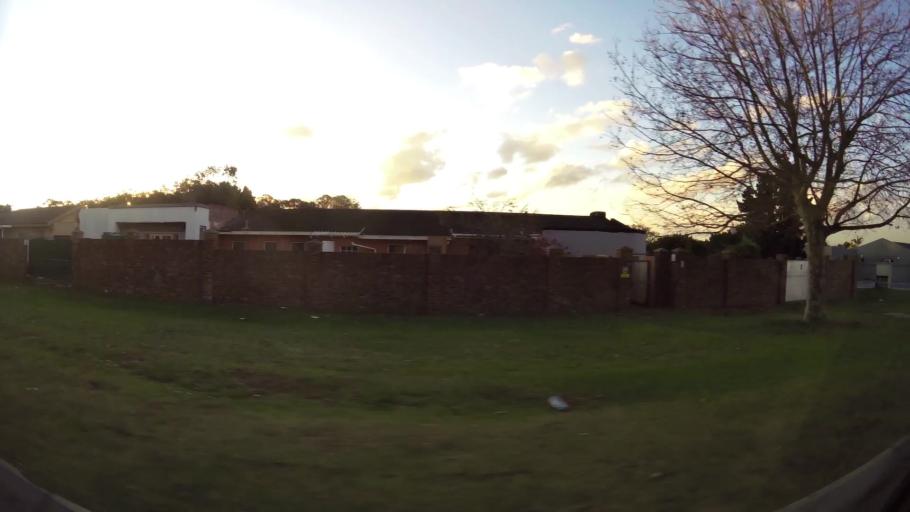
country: ZA
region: Eastern Cape
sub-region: Nelson Mandela Bay Metropolitan Municipality
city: Port Elizabeth
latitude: -33.9686
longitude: 25.5252
